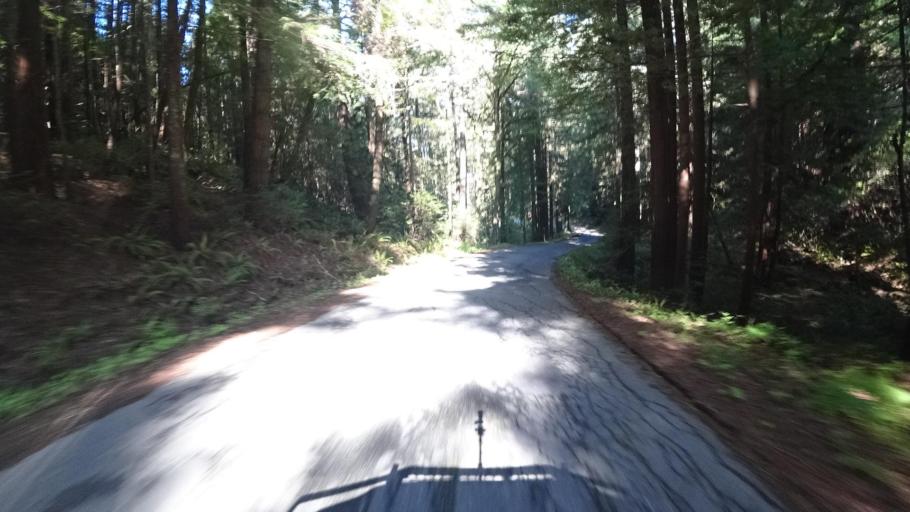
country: US
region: California
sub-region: Humboldt County
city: Rio Dell
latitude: 40.4519
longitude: -123.9837
